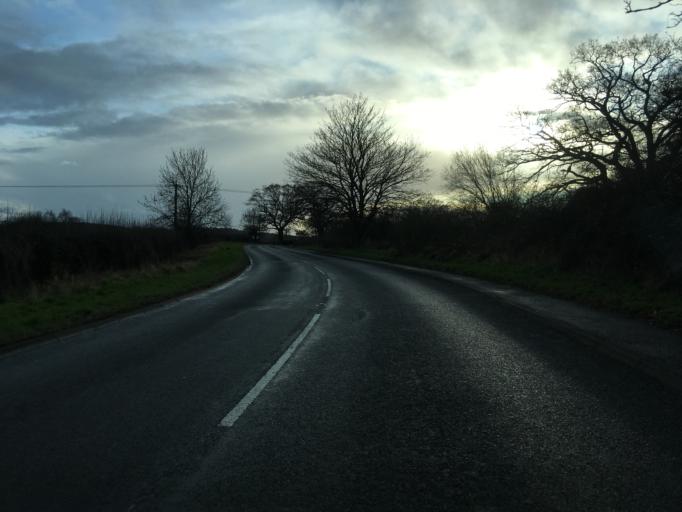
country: GB
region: England
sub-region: Warwickshire
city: Alcester
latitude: 52.2254
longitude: -1.8506
